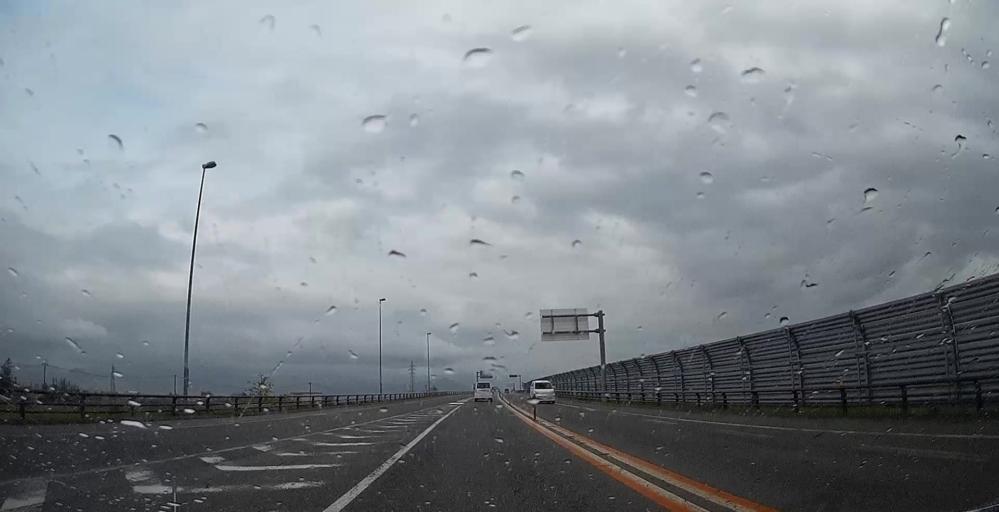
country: JP
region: Yamagata
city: Takahata
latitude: 38.0497
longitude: 140.1334
